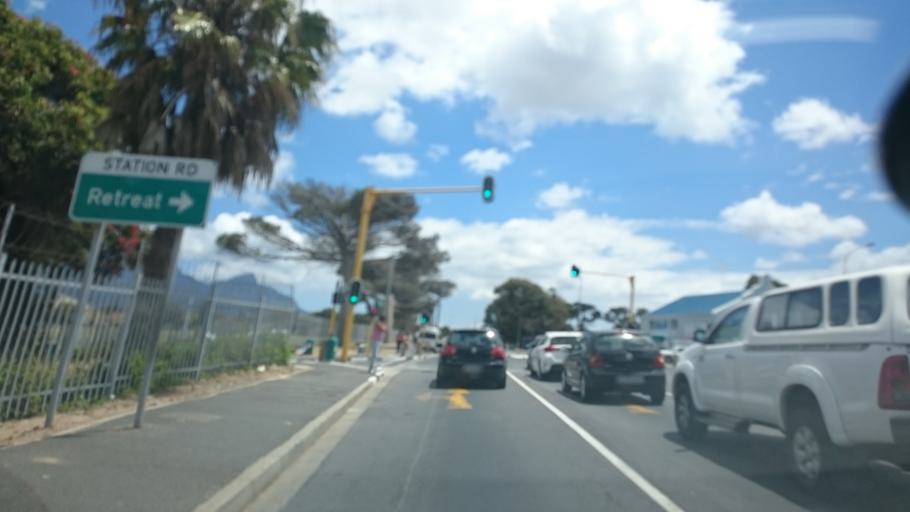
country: ZA
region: Western Cape
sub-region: City of Cape Town
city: Bergvliet
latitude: -34.0605
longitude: 18.4600
